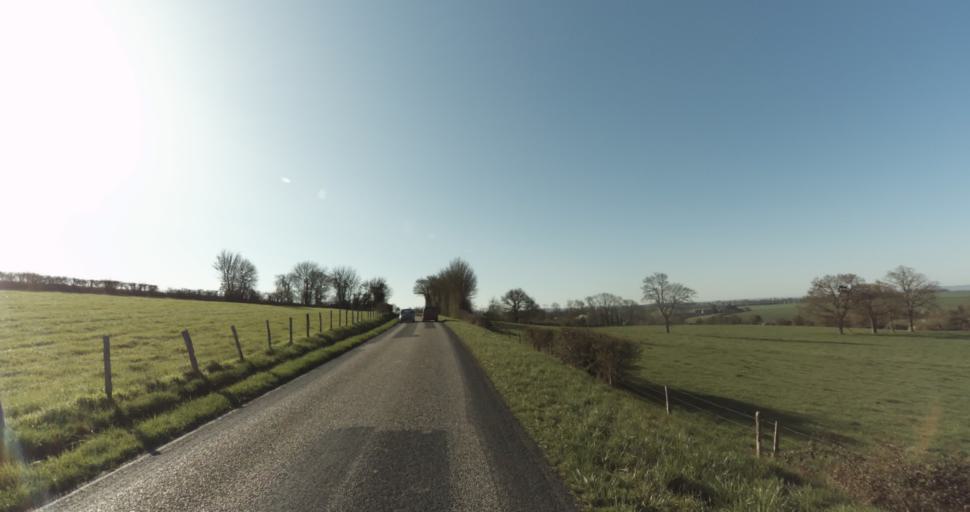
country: FR
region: Lower Normandy
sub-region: Departement du Calvados
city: Saint-Pierre-sur-Dives
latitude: 49.0108
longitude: -0.0187
